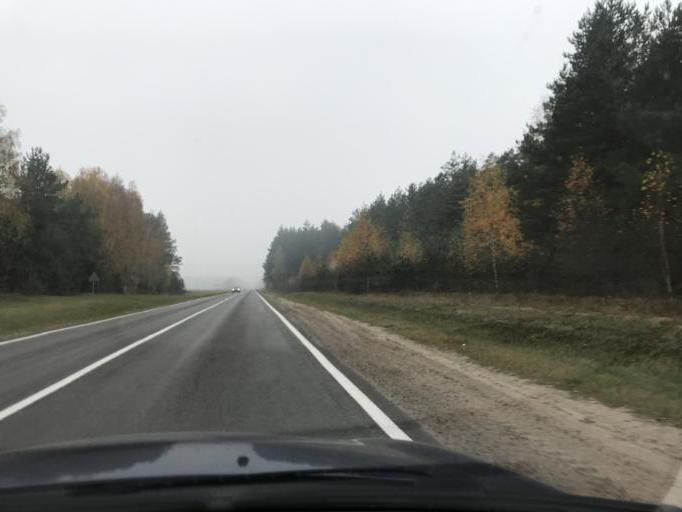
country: BY
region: Grodnenskaya
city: Hrodna
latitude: 53.7818
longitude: 23.8493
